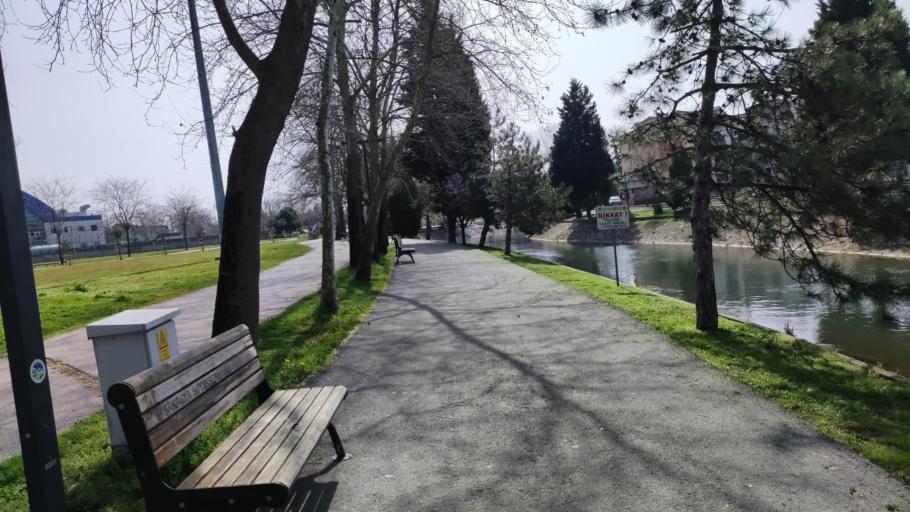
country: TR
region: Sakarya
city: Adapazari
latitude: 40.7743
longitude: 30.3858
